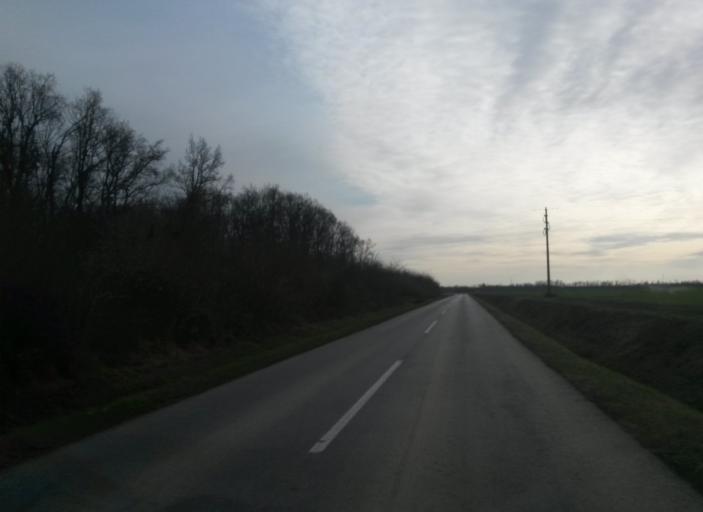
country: HR
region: Osjecko-Baranjska
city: Ovcara
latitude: 45.5103
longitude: 18.5949
